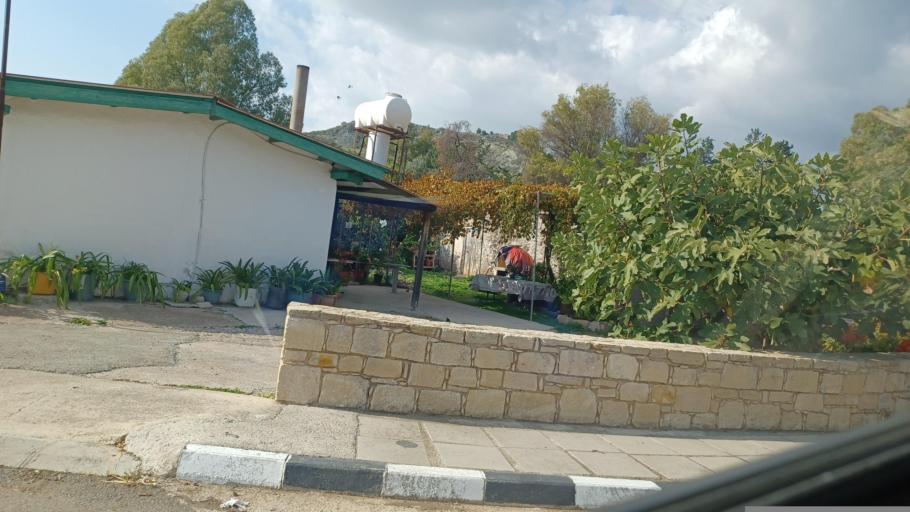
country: CY
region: Limassol
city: Pissouri
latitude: 34.7614
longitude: 32.6256
